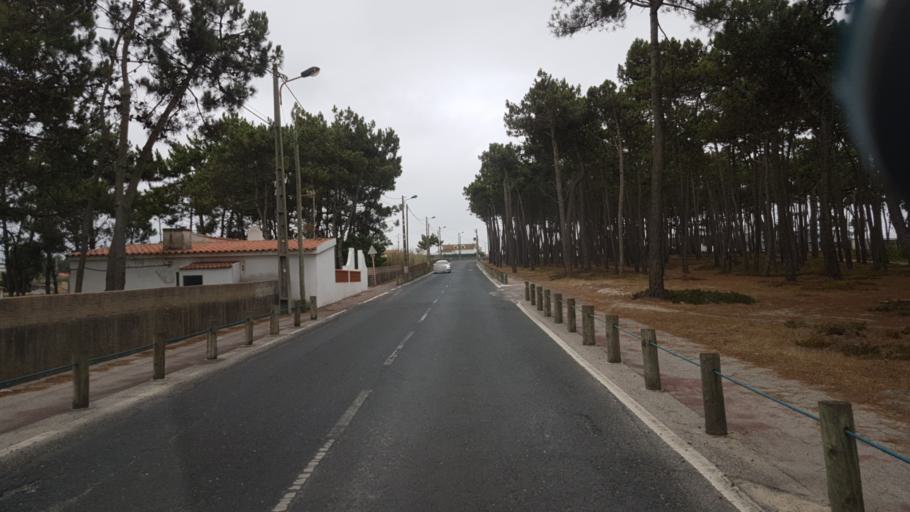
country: PT
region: Lisbon
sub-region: Torres Vedras
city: Silveira
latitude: 39.1558
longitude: -9.3611
